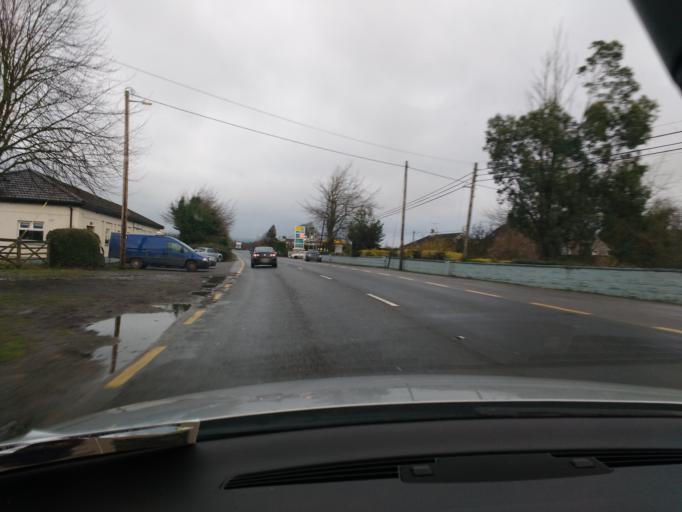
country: IE
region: Munster
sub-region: North Tipperary
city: Templemore
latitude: 52.7218
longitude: -7.9120
